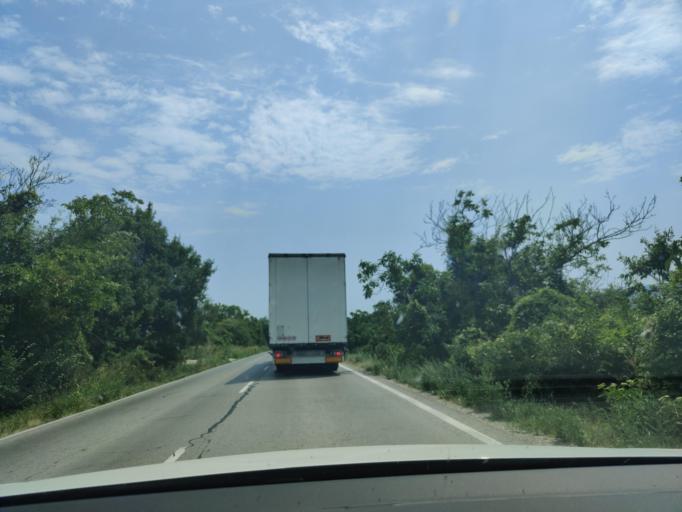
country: BG
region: Vidin
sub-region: Obshtina Ruzhintsi
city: Ruzhintsi
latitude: 43.6378
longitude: 22.8043
